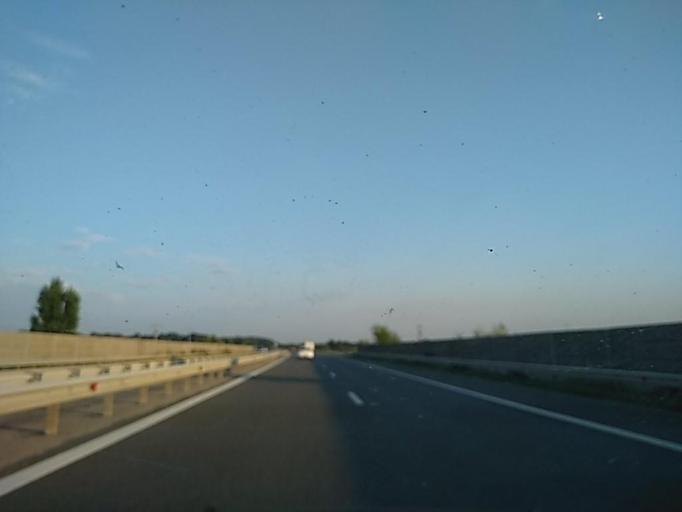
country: RO
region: Prahova
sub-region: Comuna Rafov
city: Rafov
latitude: 44.8748
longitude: 26.1369
